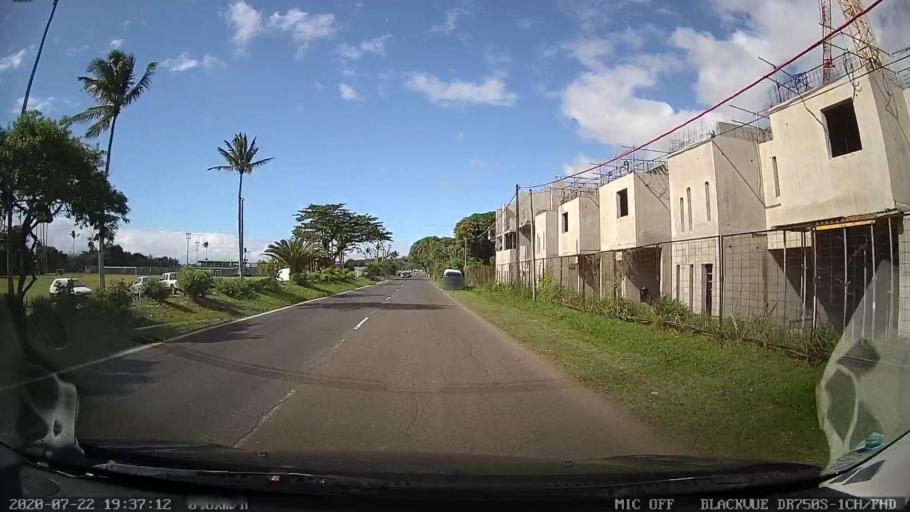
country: RE
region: Reunion
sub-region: Reunion
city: Sainte-Suzanne
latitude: -20.9111
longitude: 55.6117
